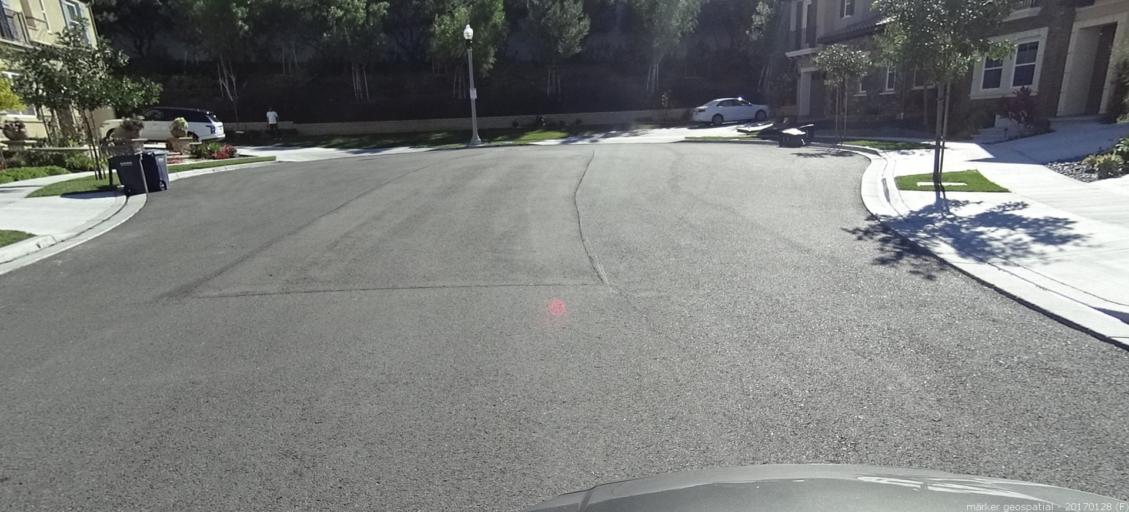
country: US
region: California
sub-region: Orange County
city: Lake Forest
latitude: 33.6700
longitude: -117.6841
